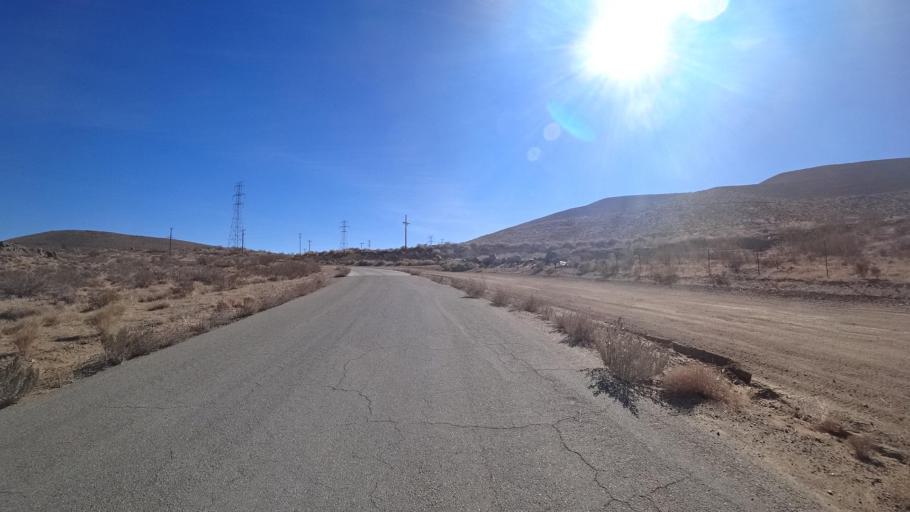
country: US
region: California
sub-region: Kern County
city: Ridgecrest
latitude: 35.3564
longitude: -117.6455
